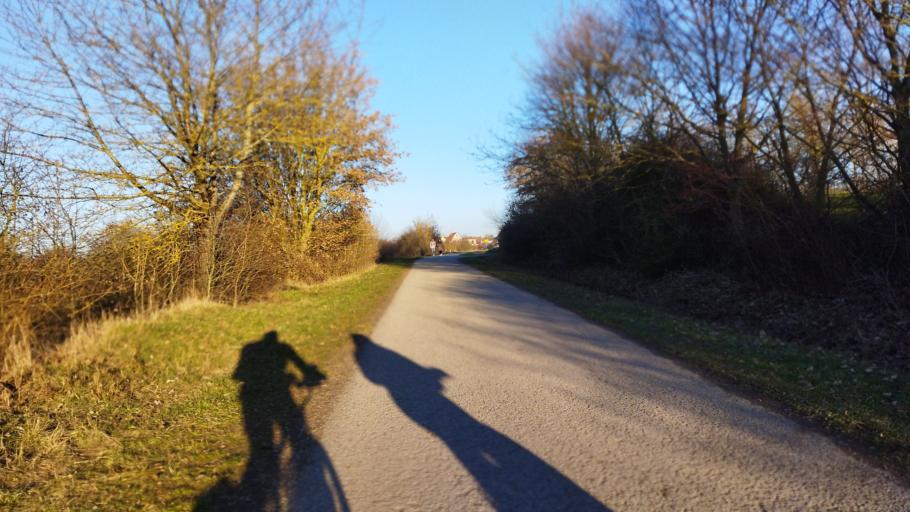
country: DE
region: Bavaria
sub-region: Regierungsbezirk Unterfranken
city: Dettelbach
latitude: 49.7921
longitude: 10.1612
